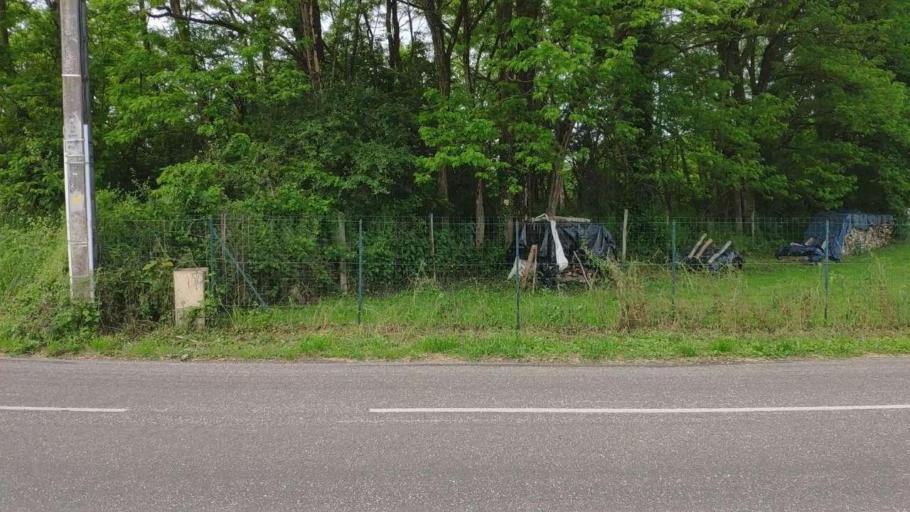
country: FR
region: Franche-Comte
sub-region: Departement du Jura
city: Perrigny
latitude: 46.7702
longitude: 5.5912
